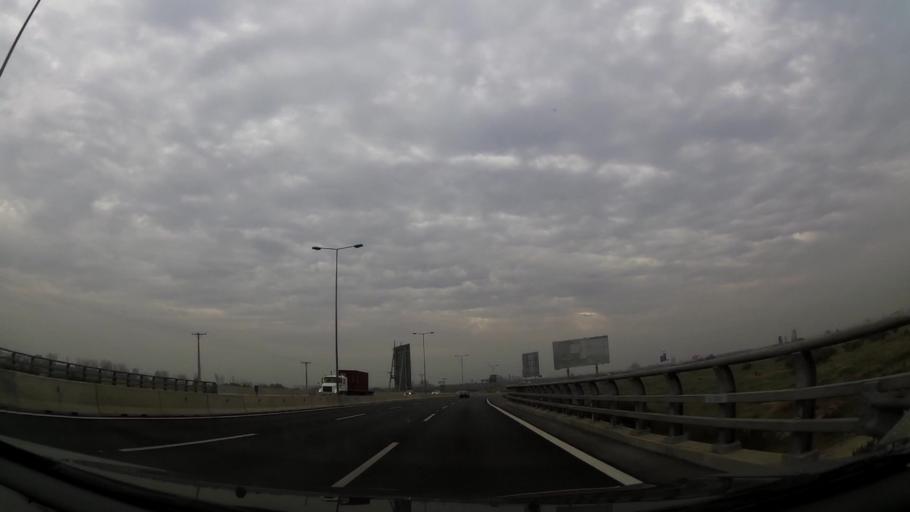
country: CL
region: Santiago Metropolitan
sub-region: Provincia de Santiago
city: Lo Prado
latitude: -33.4169
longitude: -70.7891
